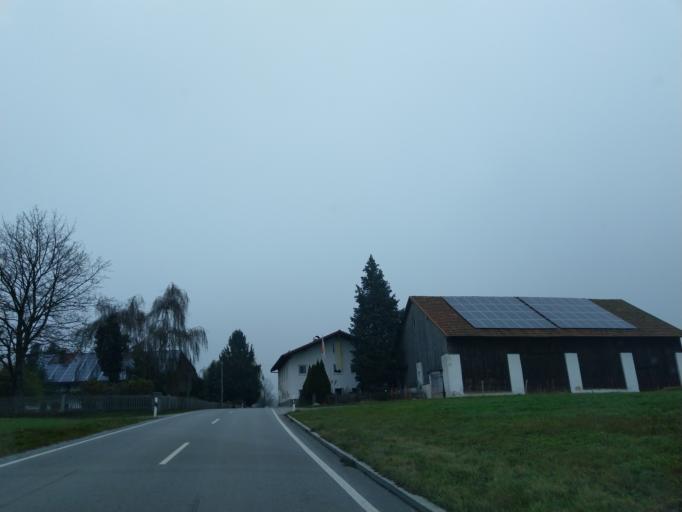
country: DE
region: Bavaria
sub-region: Lower Bavaria
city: Schollnach
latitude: 48.7596
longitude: 13.1862
